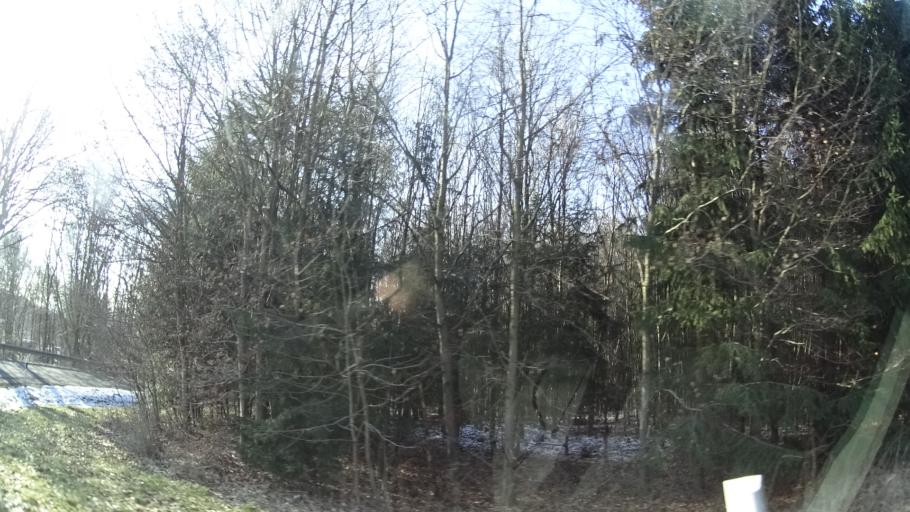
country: DE
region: Hesse
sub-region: Regierungsbezirk Kassel
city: Flieden
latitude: 50.3723
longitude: 9.5848
